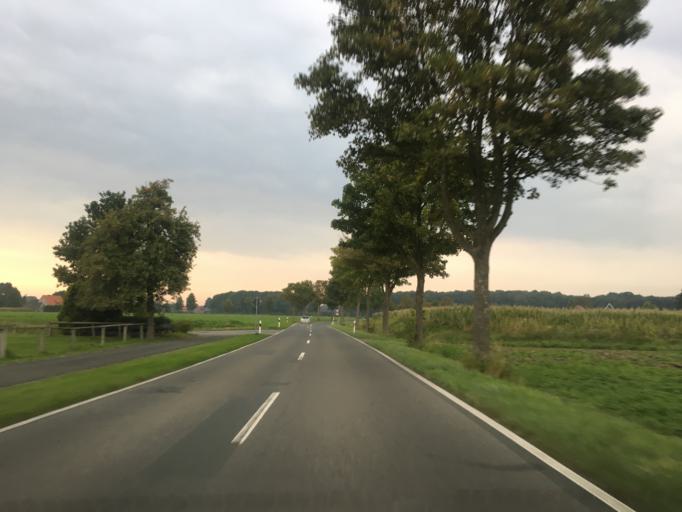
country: DE
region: North Rhine-Westphalia
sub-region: Regierungsbezirk Munster
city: Ascheberg
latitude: 51.7909
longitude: 7.5958
